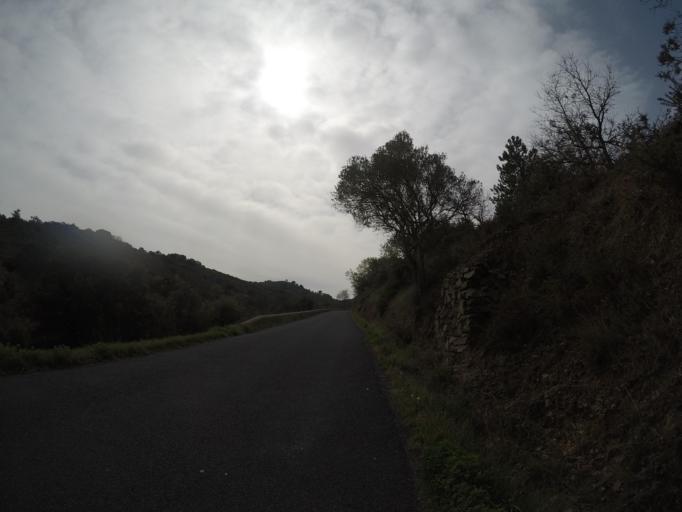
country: FR
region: Languedoc-Roussillon
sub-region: Departement des Pyrenees-Orientales
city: Estagel
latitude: 42.7482
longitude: 2.7241
